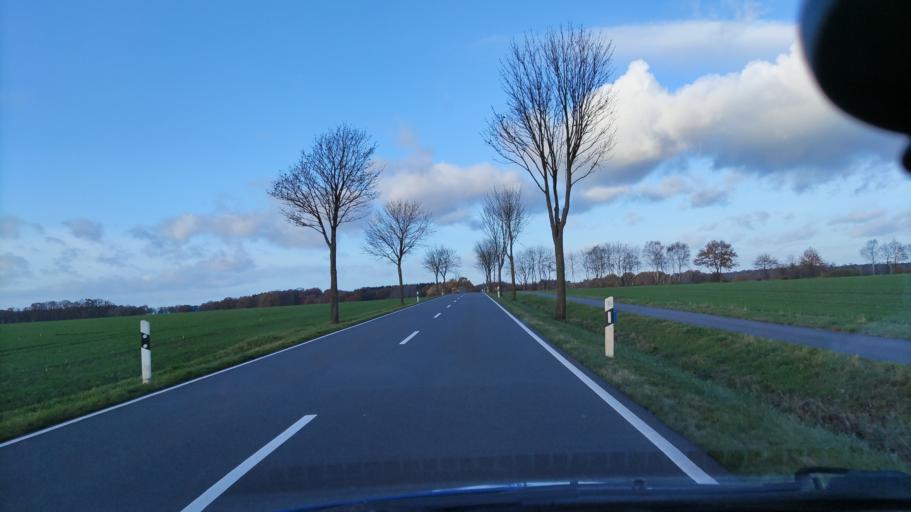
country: DE
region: Lower Saxony
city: Schneverdingen
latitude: 53.0639
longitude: 9.8172
